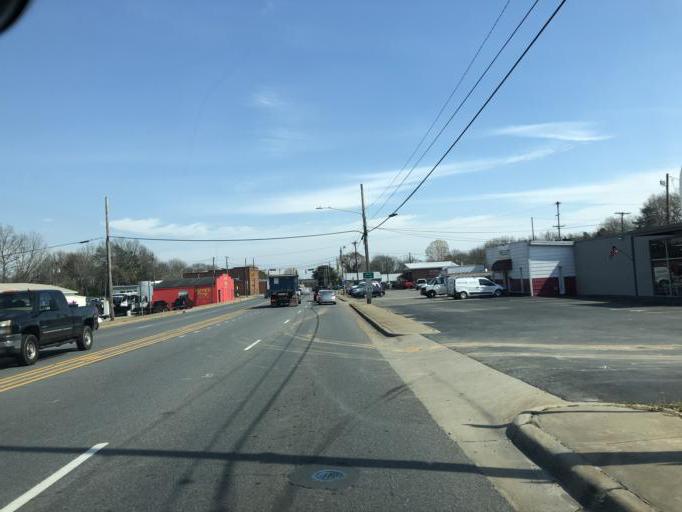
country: US
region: North Carolina
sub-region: Gaston County
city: Ranlo
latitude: 35.2794
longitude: -81.1359
